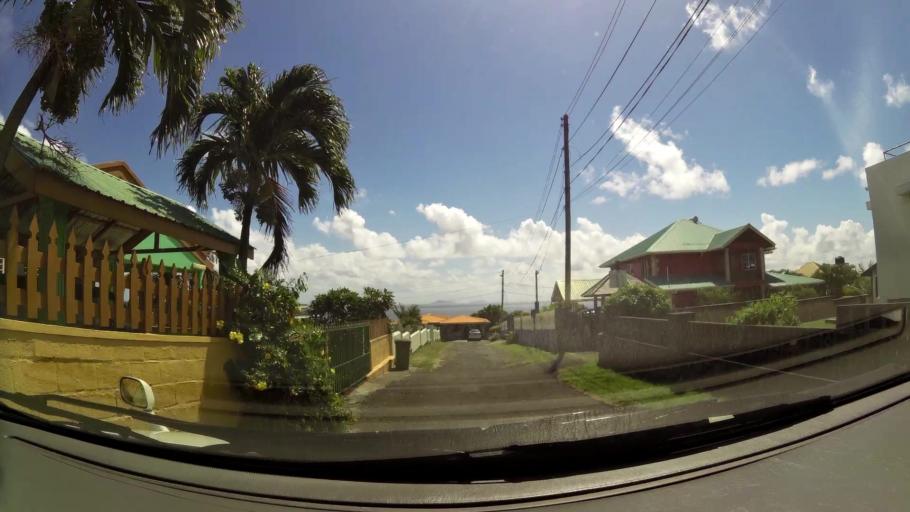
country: VC
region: Saint George
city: Kingstown
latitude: 13.1396
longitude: -61.2241
